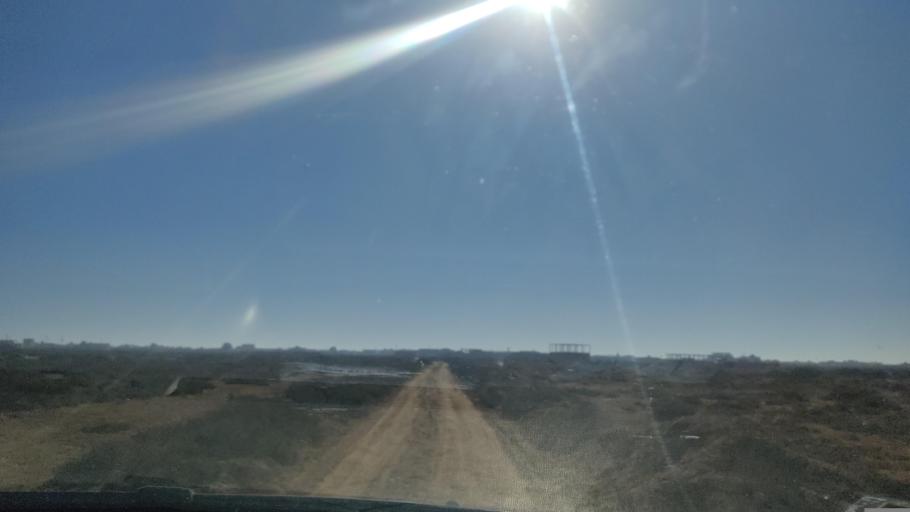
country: TN
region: Safaqis
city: Al Qarmadah
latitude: 34.8132
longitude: 10.8574
